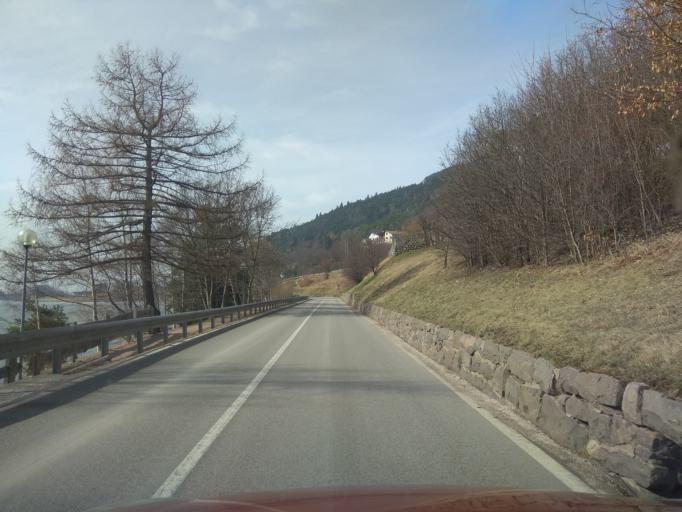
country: IT
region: Trentino-Alto Adige
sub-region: Provincia di Trento
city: Segonzano
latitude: 46.1566
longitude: 11.2813
